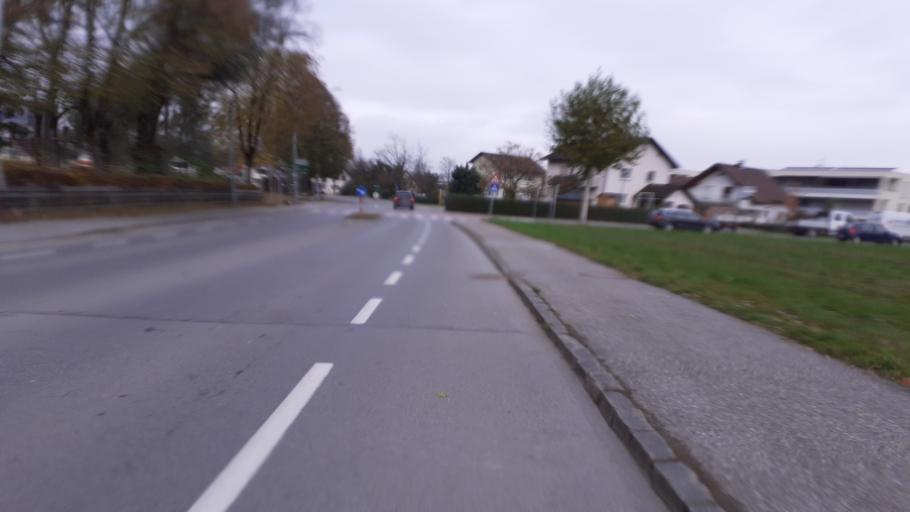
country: AT
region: Vorarlberg
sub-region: Politischer Bezirk Feldkirch
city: Nofels
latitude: 47.2538
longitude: 9.5869
